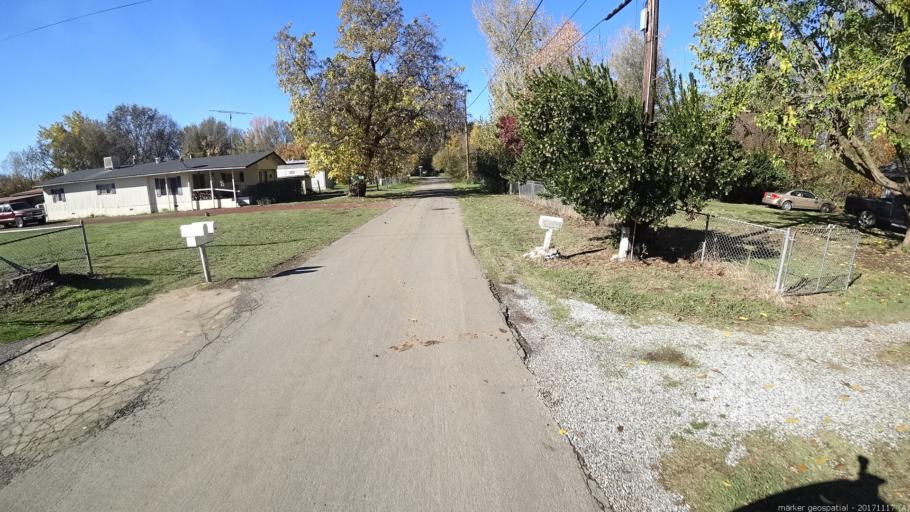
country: US
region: California
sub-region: Shasta County
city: Anderson
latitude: 40.4462
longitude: -122.2359
